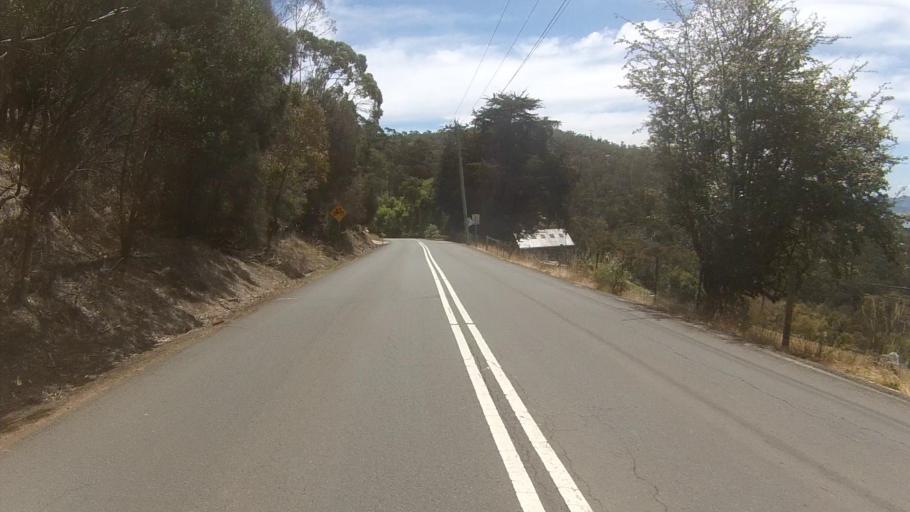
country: AU
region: Tasmania
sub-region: Kingborough
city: Kingston Beach
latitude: -42.9634
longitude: 147.3316
